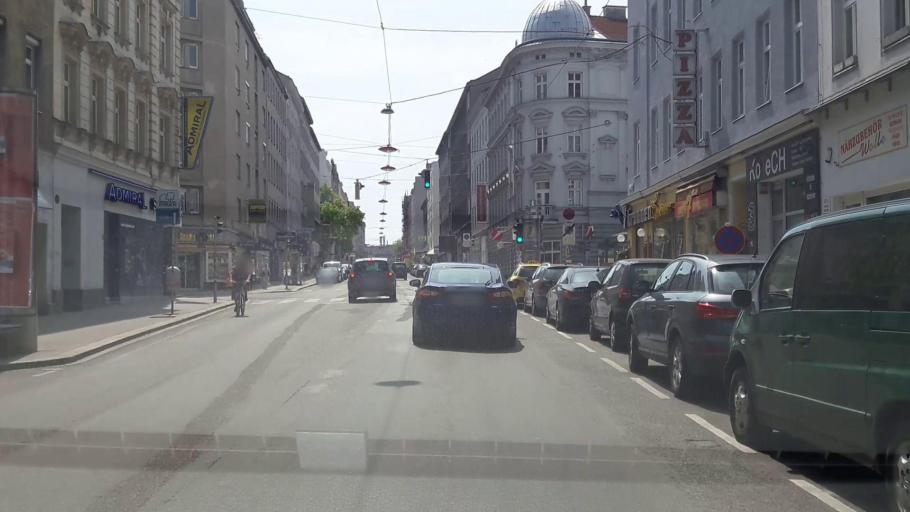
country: AT
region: Vienna
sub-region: Wien Stadt
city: Vienna
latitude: 48.1861
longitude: 16.3537
